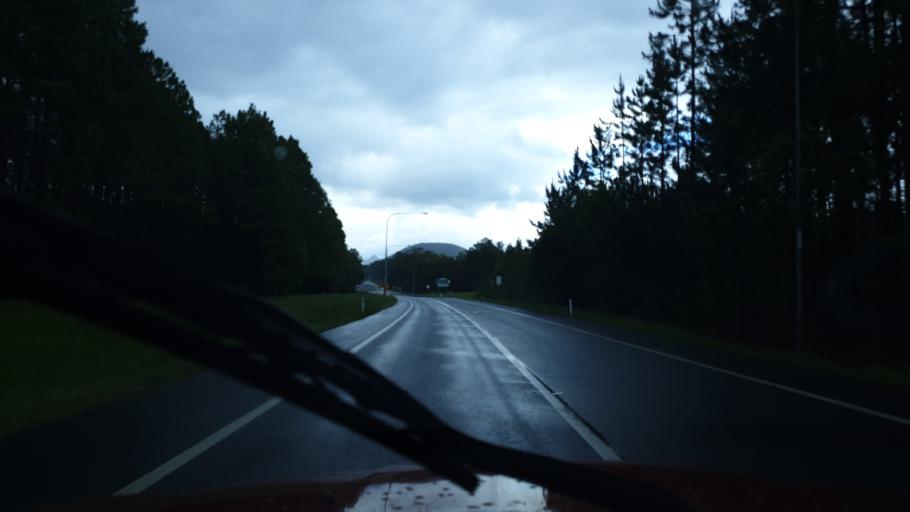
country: AU
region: Queensland
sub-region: Moreton Bay
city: Caboolture
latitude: -26.9871
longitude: 152.9752
